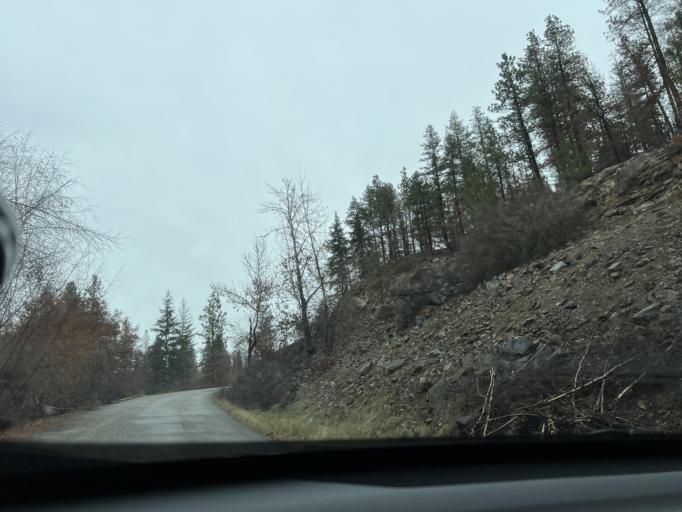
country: US
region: Washington
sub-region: Okanogan County
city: Brewster
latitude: 48.5656
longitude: -120.1761
